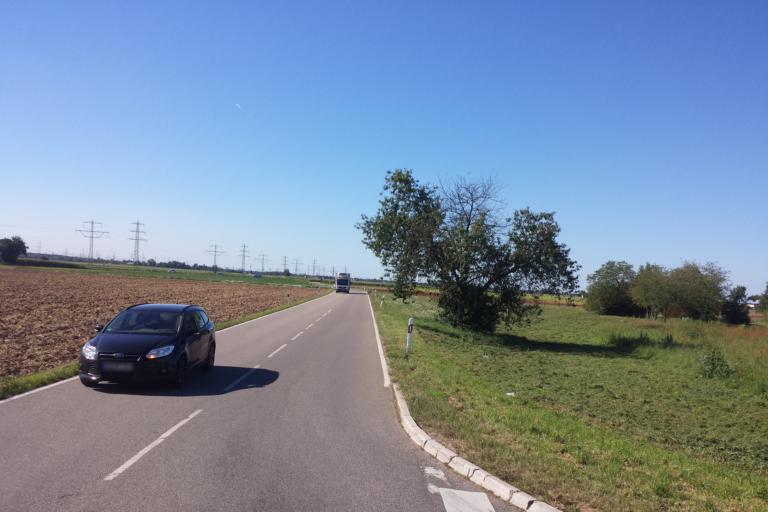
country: DE
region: Baden-Wuerttemberg
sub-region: Karlsruhe Region
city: Eppelheim
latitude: 49.4062
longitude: 8.6181
